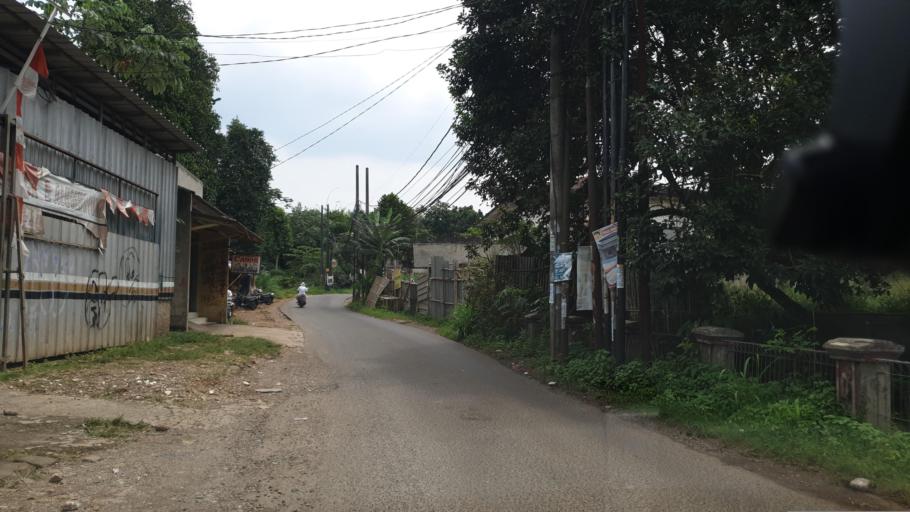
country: ID
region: West Java
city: Pamulang
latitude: -6.3668
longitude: 106.7617
